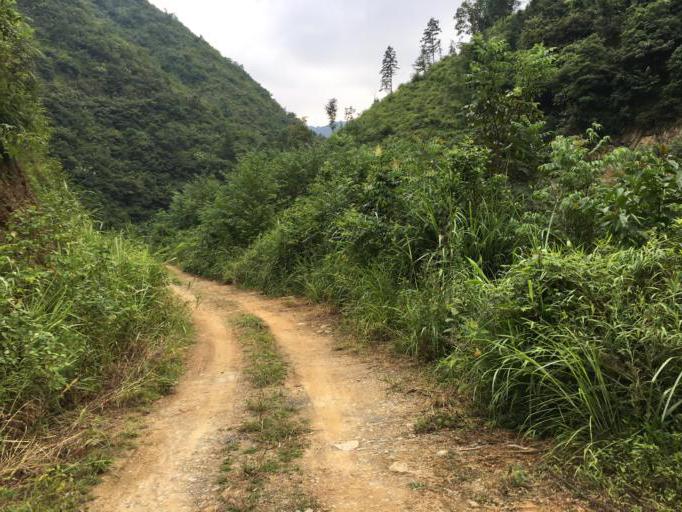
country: CN
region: Guangxi Zhuangzu Zizhiqu
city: Tongle
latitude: 25.2981
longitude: 106.1426
